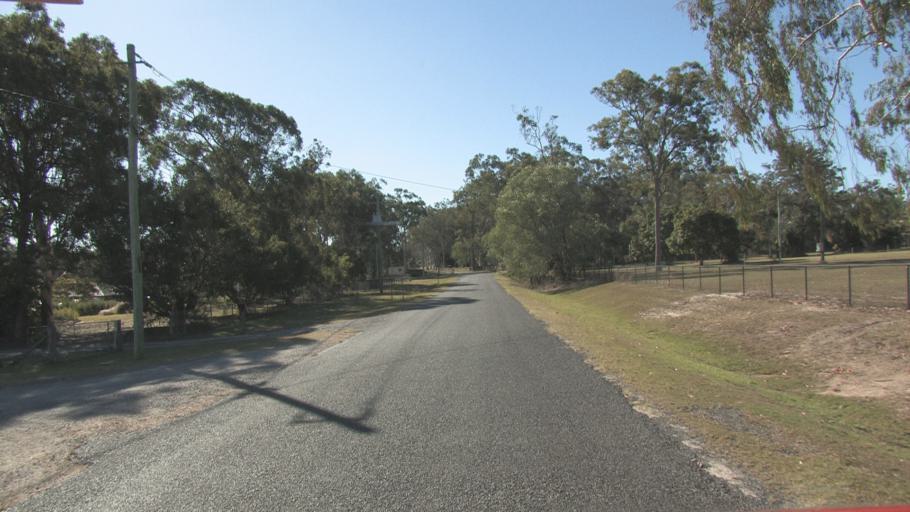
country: AU
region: Queensland
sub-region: Logan
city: Chambers Flat
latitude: -27.7359
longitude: 153.0779
